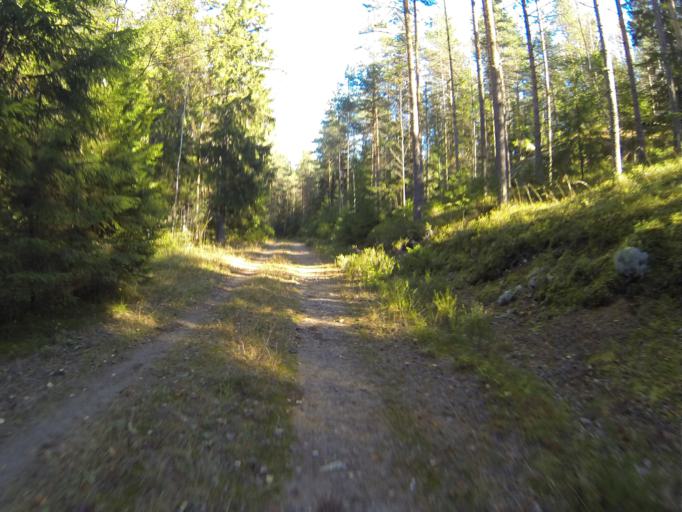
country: FI
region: Varsinais-Suomi
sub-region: Salo
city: Saerkisalo
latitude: 60.2083
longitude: 22.9606
